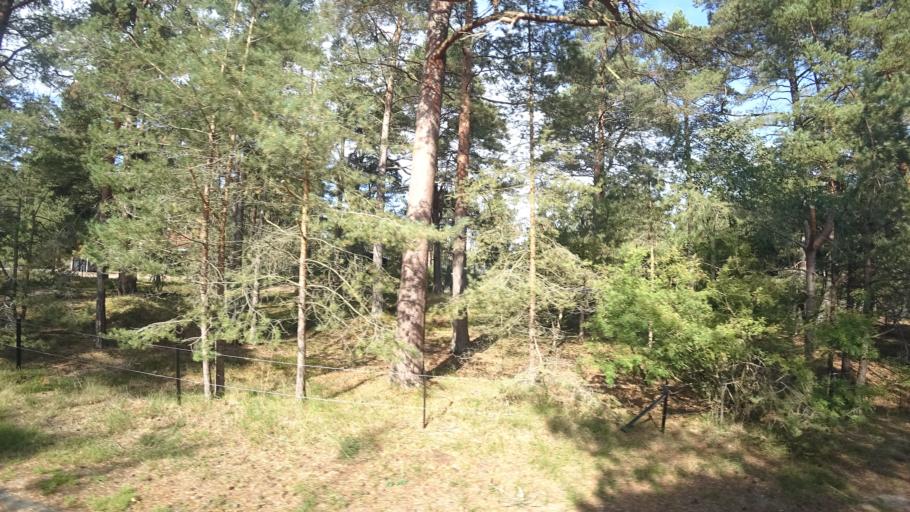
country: SE
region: Skane
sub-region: Kristianstads Kommun
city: Ahus
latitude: 55.9072
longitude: 14.2900
